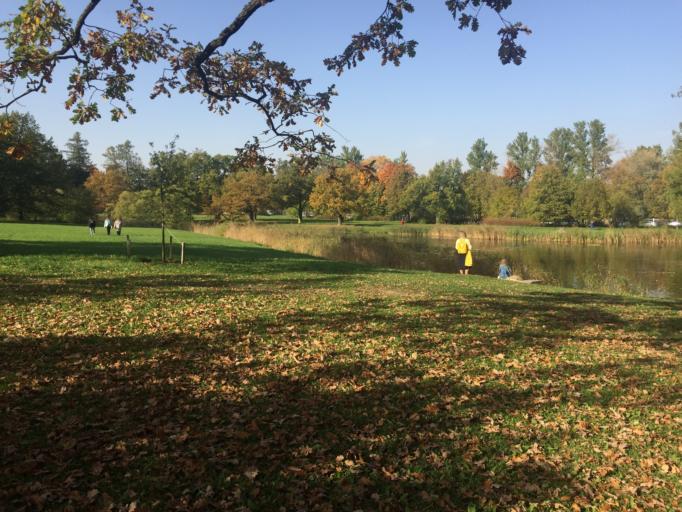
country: RU
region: St.-Petersburg
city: Pushkin
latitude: 59.7216
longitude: 30.3946
